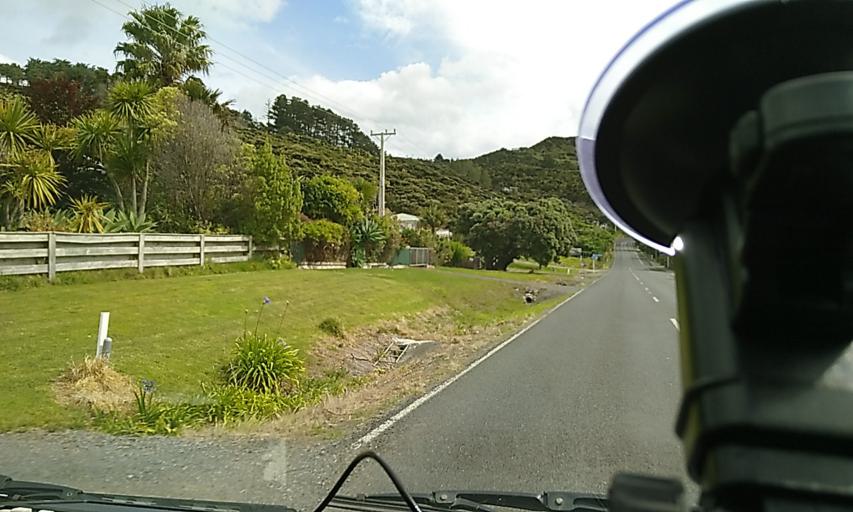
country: NZ
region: Northland
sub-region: Far North District
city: Ahipara
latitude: -35.5344
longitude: 173.3881
